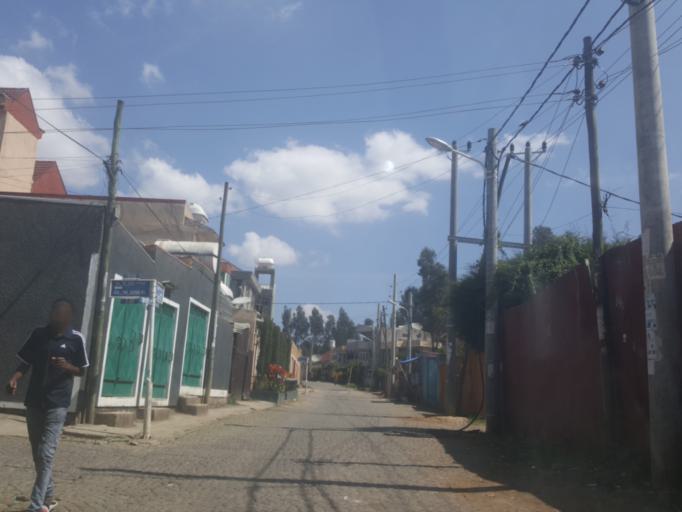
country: ET
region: Adis Abeba
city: Addis Ababa
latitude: 9.0665
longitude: 38.7189
